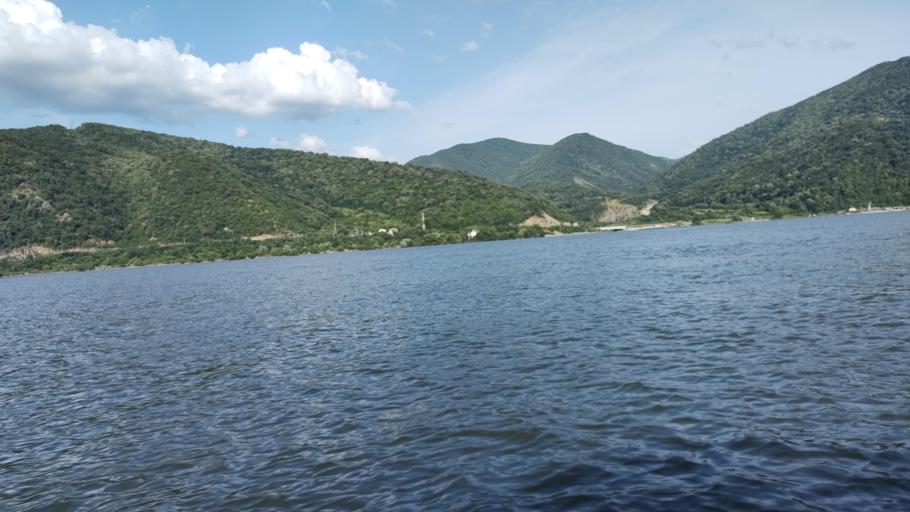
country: RO
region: Caras-Severin
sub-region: Comuna Berzasca
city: Berzasca
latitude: 44.6242
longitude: 21.9968
